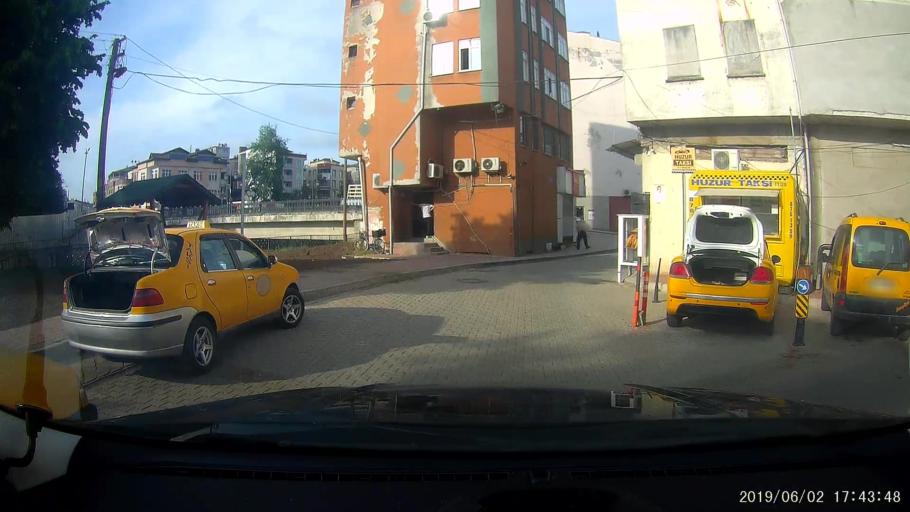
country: TR
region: Samsun
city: Terme
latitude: 41.2076
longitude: 36.9721
